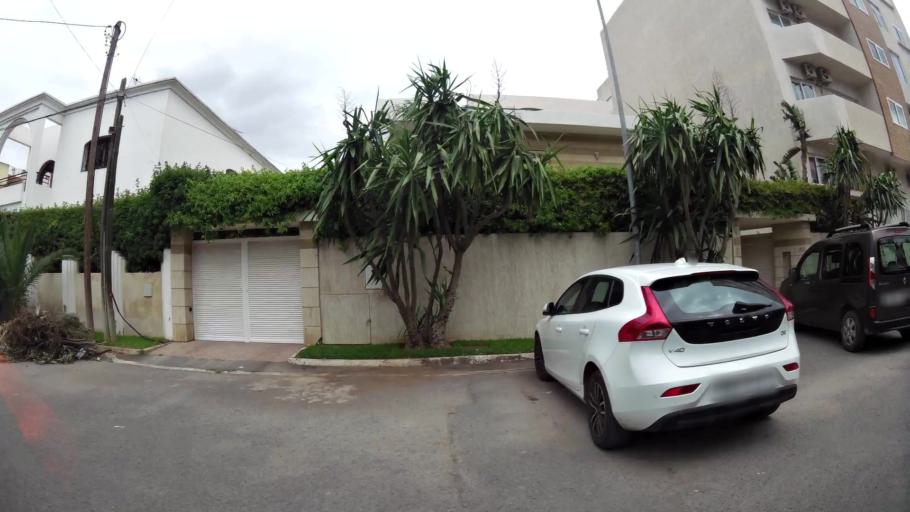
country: MA
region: Grand Casablanca
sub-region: Casablanca
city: Casablanca
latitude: 33.5503
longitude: -7.6420
